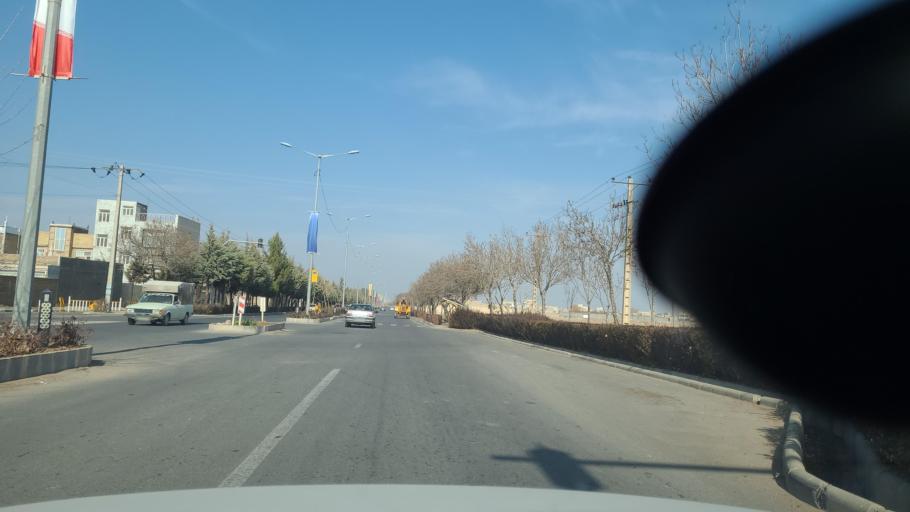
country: IR
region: Razavi Khorasan
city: Fariman
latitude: 35.6844
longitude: 59.8434
